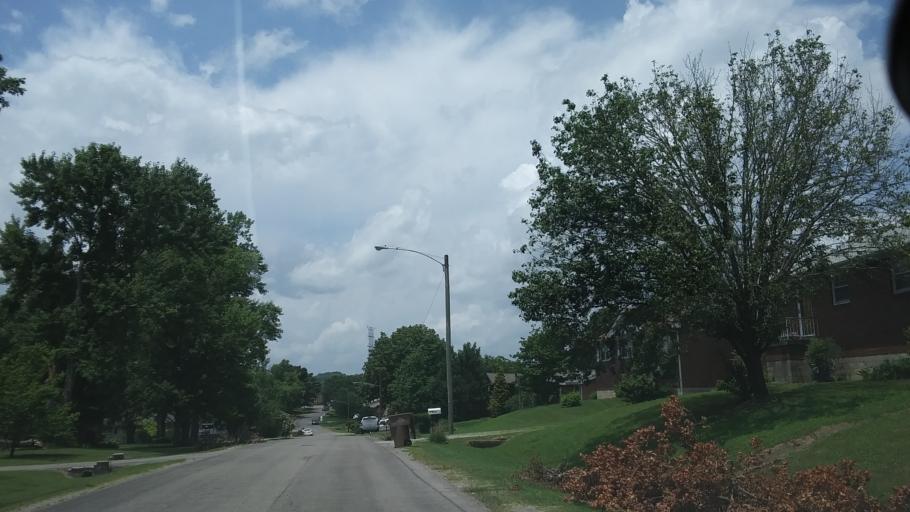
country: US
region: Tennessee
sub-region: Davidson County
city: Belle Meade
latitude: 36.1453
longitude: -86.8857
